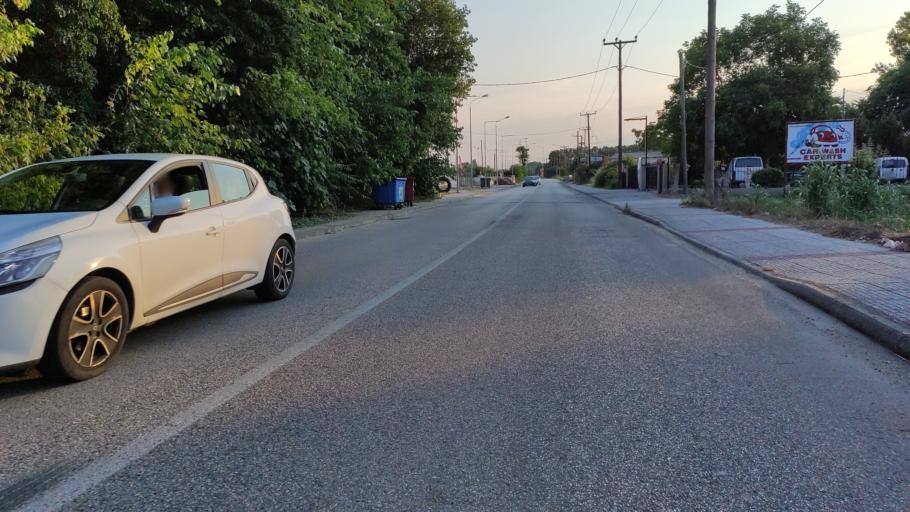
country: GR
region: East Macedonia and Thrace
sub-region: Nomos Rodopis
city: Komotini
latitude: 41.1156
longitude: 25.3831
